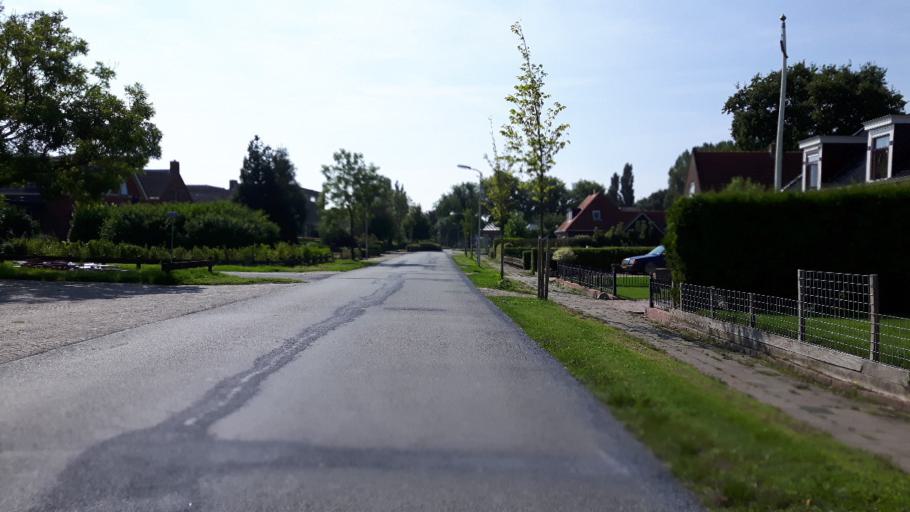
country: NL
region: Friesland
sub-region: Gemeente Ferwerderadiel
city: Marrum
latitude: 53.3271
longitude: 5.8038
